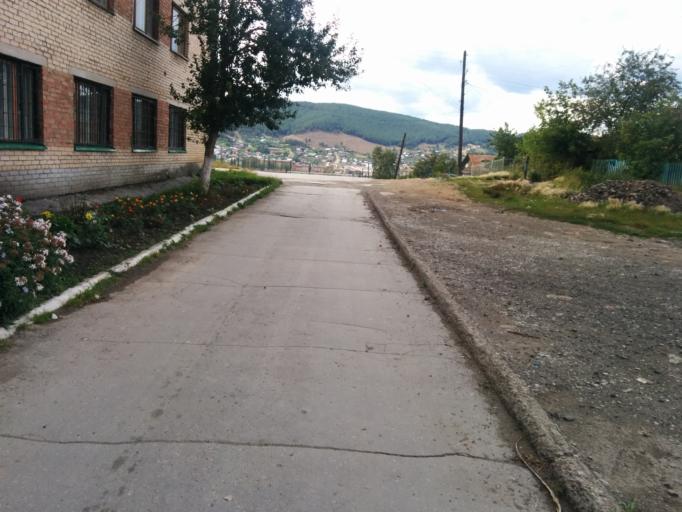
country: RU
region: Bashkortostan
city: Beloretsk
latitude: 53.9719
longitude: 58.4065
